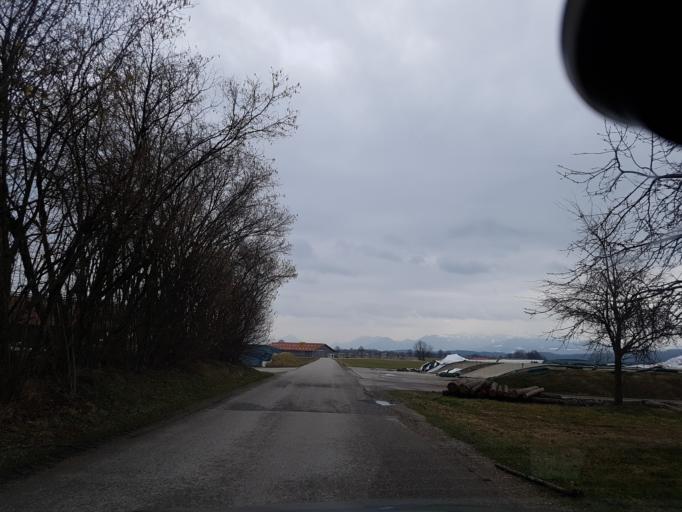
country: DE
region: Bavaria
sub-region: Upper Bavaria
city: Bruckmuhl
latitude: 47.9057
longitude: 11.9189
